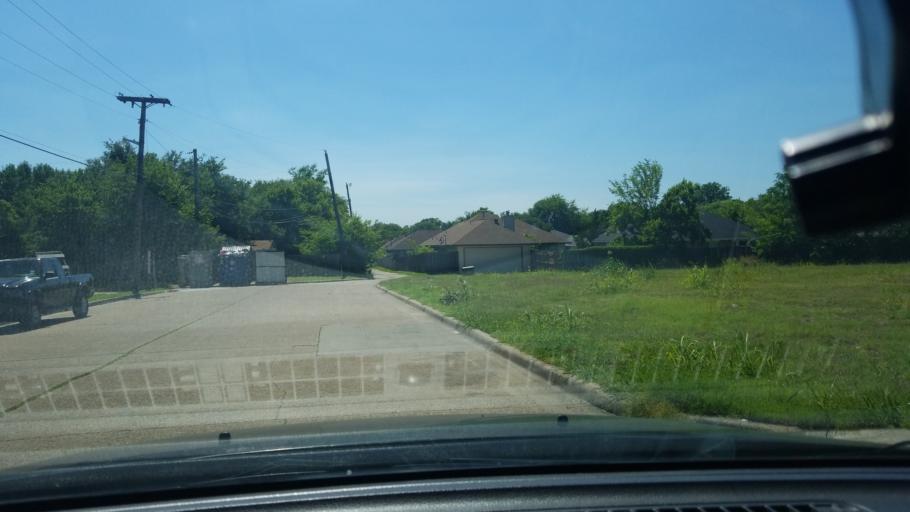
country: US
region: Texas
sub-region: Dallas County
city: Mesquite
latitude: 32.7783
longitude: -96.6031
